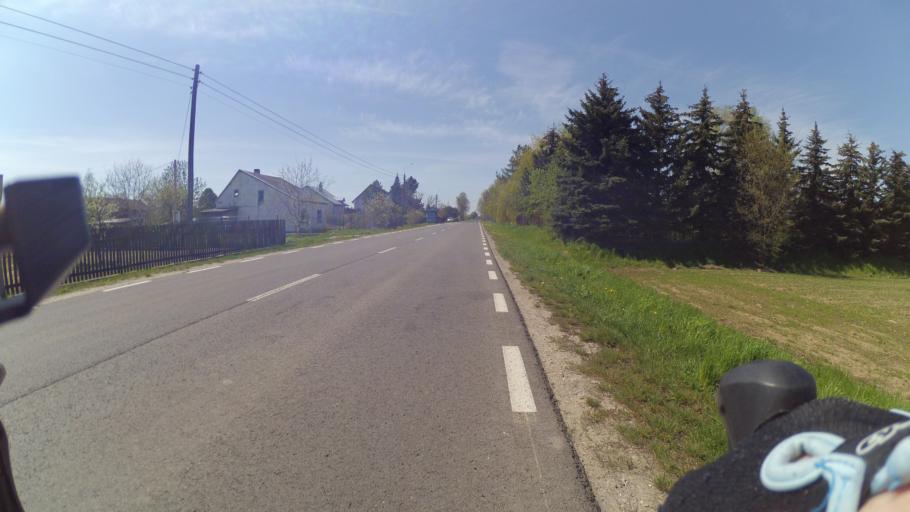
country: PL
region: Masovian Voivodeship
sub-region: Powiat plonski
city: Czerwinsk Nad Wisla
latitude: 52.3778
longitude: 20.3381
